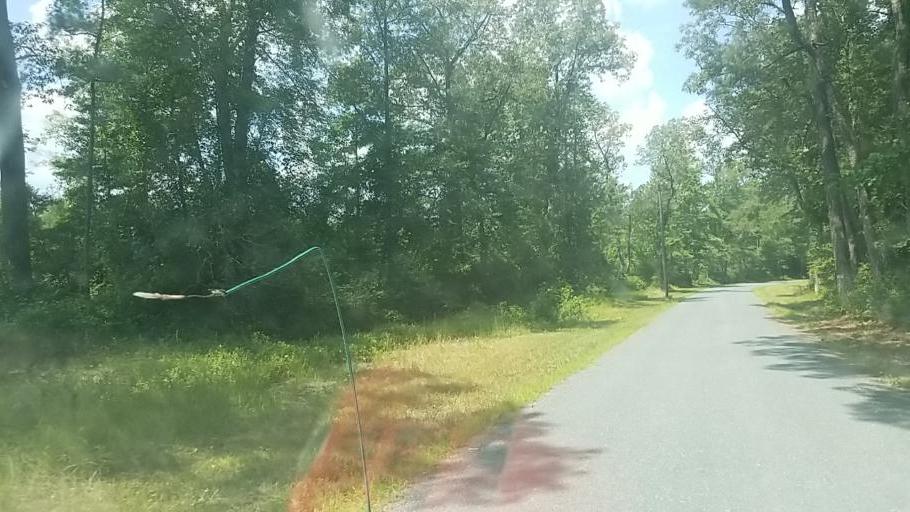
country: US
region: Maryland
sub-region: Worcester County
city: Snow Hill
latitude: 38.2482
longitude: -75.4192
